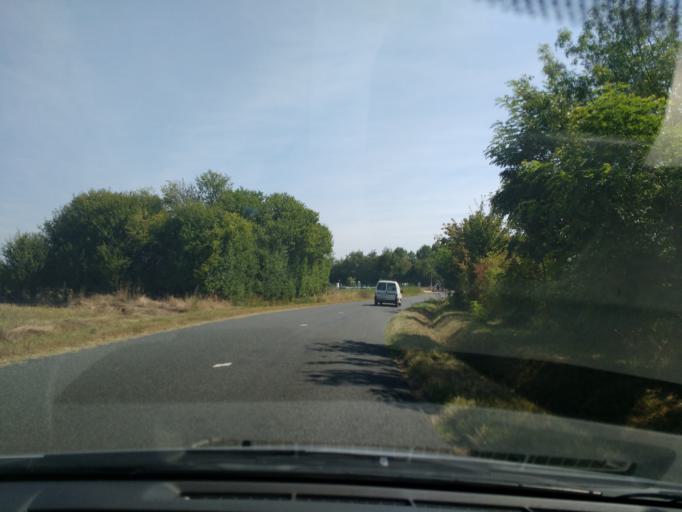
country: FR
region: Pays de la Loire
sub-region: Departement de Maine-et-Loire
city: Maze
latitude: 47.4794
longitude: -0.2386
